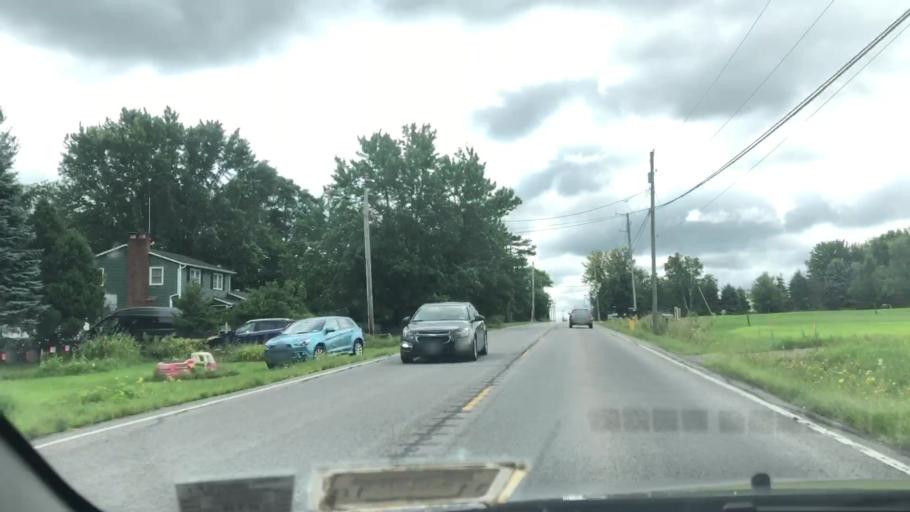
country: US
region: New York
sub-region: Wayne County
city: Macedon
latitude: 43.1119
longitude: -77.2930
